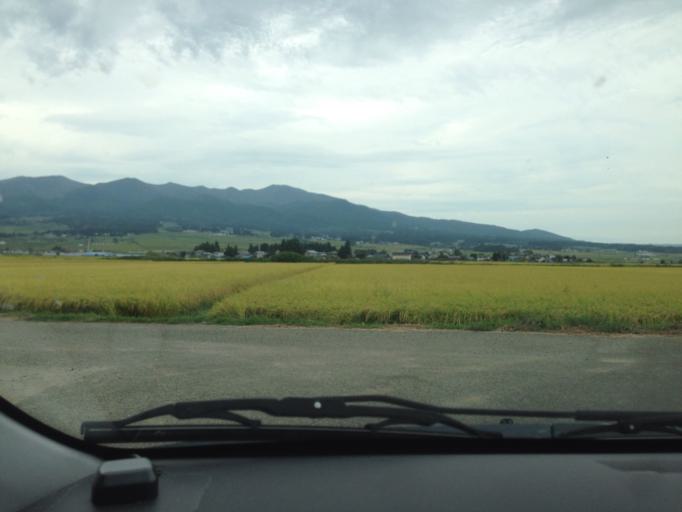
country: JP
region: Fukushima
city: Kitakata
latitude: 37.6318
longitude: 139.9017
